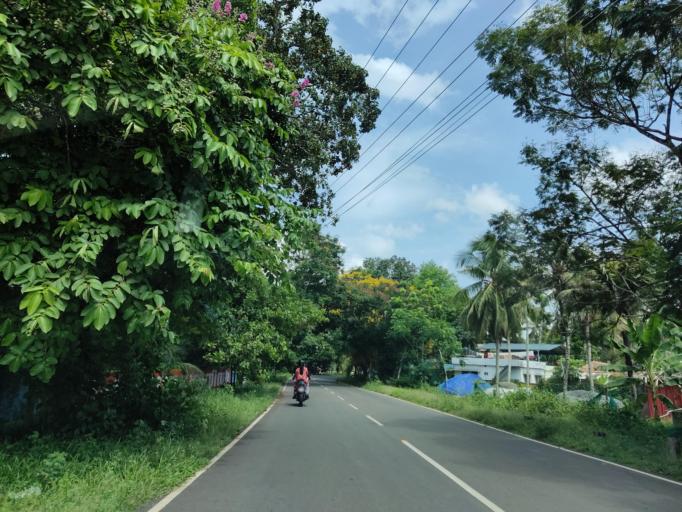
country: IN
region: Kerala
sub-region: Alappuzha
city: Mavelikara
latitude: 9.2710
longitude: 76.5664
